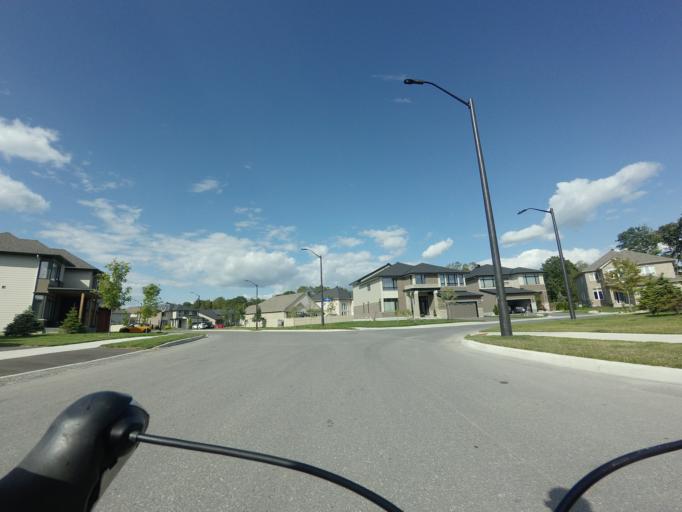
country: CA
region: Ontario
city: Bells Corners
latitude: 45.2863
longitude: -75.8425
